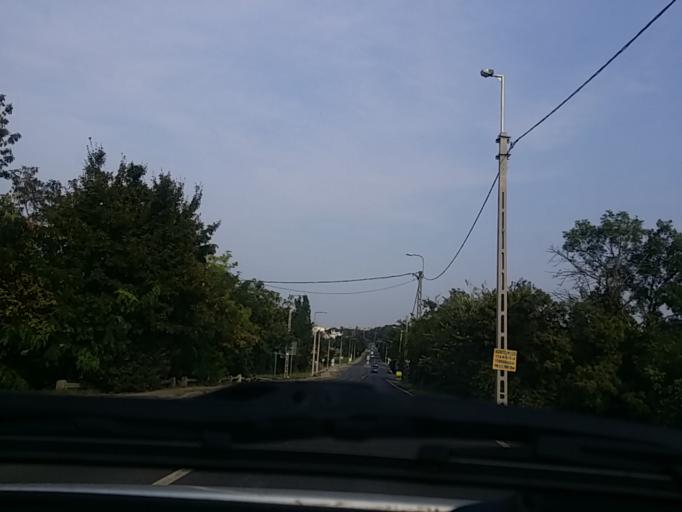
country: HU
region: Pest
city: Budaors
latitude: 47.4624
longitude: 18.9906
